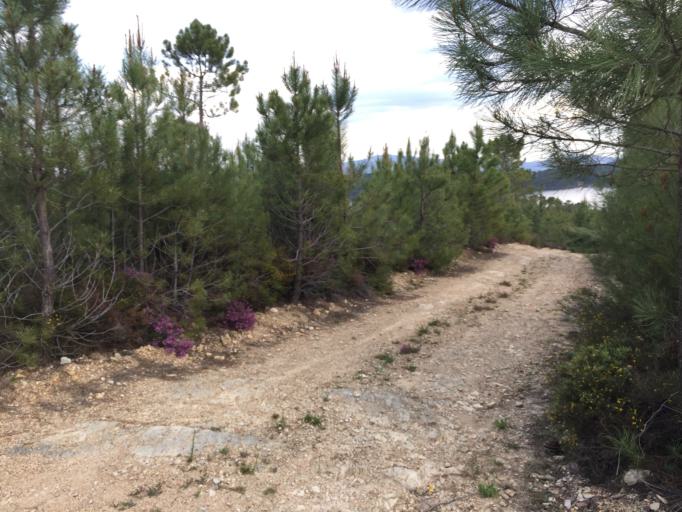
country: PT
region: Coimbra
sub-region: Pampilhosa da Serra
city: Pampilhosa da Serra
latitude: 40.1030
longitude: -7.8660
